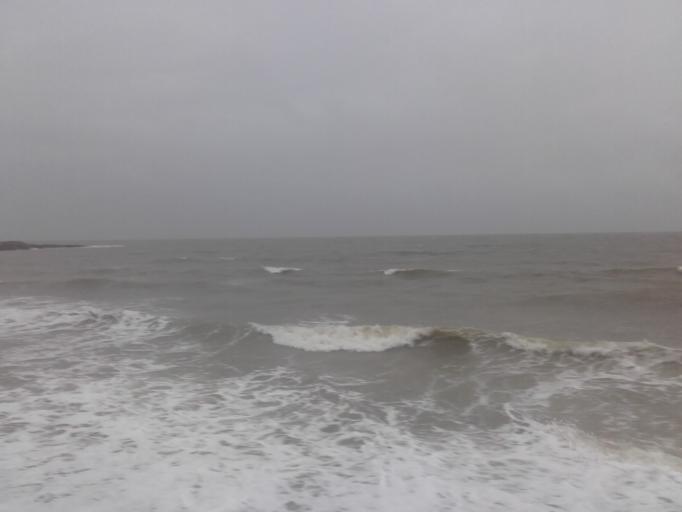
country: FR
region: Brittany
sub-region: Departement du Morbihan
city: Sarzeau
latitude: 47.4948
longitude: -2.6819
